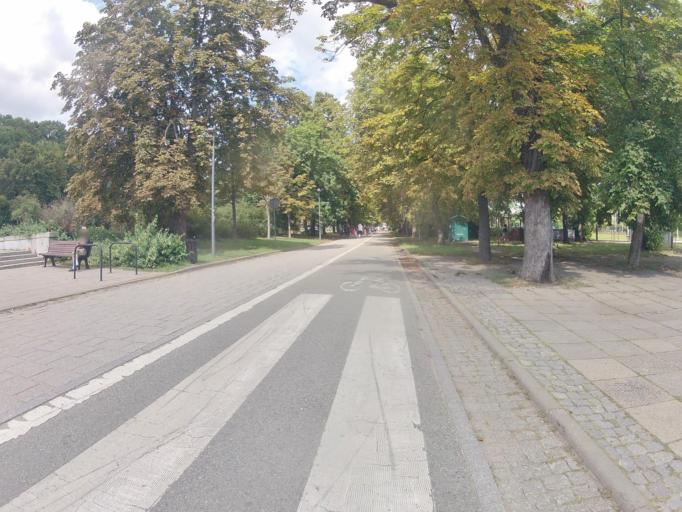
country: PL
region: Masovian Voivodeship
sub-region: Warszawa
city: Srodmiescie
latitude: 52.2194
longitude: 21.0332
